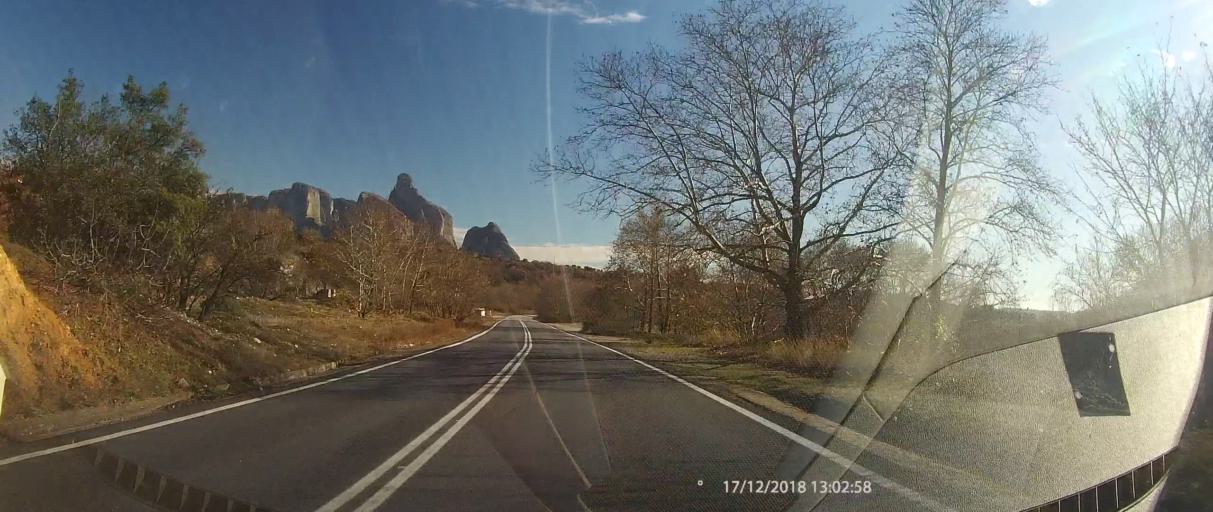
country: GR
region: Thessaly
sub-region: Trikala
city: Kastraki
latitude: 39.7168
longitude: 21.5971
